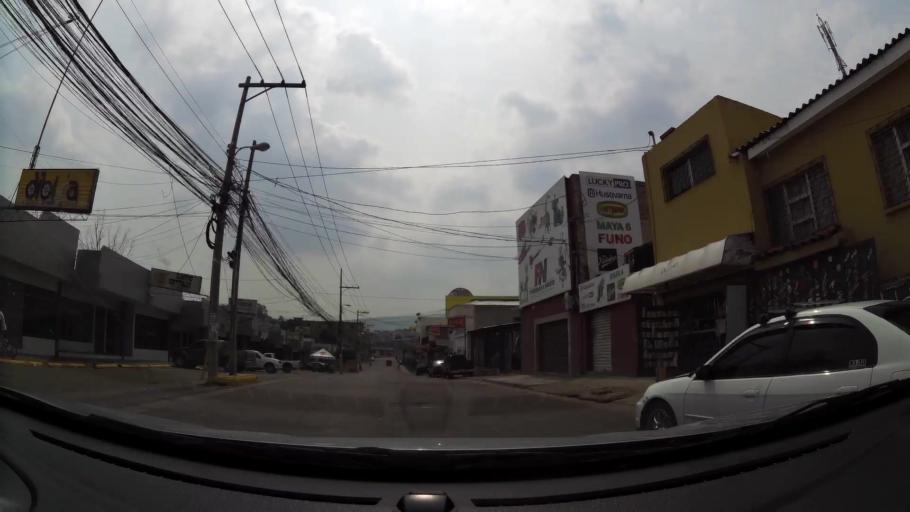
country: HN
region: Francisco Morazan
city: Tegucigalpa
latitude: 14.0931
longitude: -87.2131
